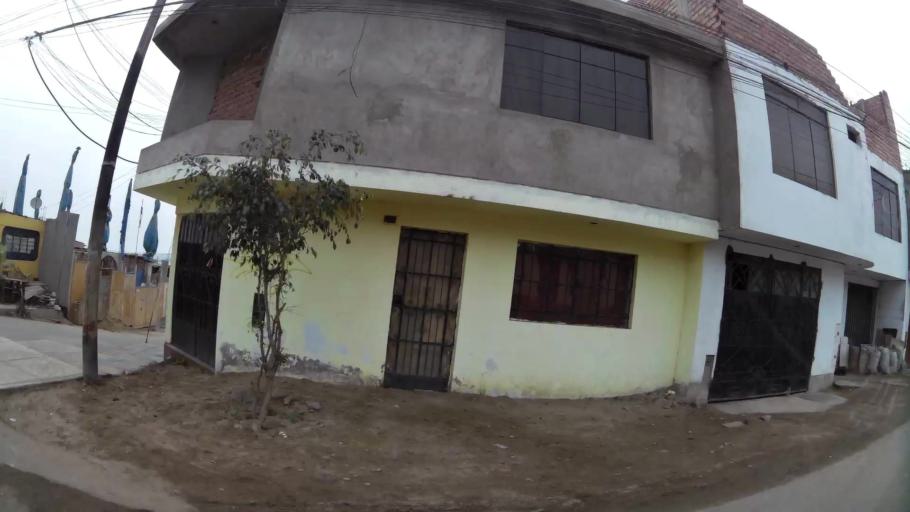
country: PE
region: Lima
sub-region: Lima
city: Surco
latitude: -12.1770
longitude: -76.9612
